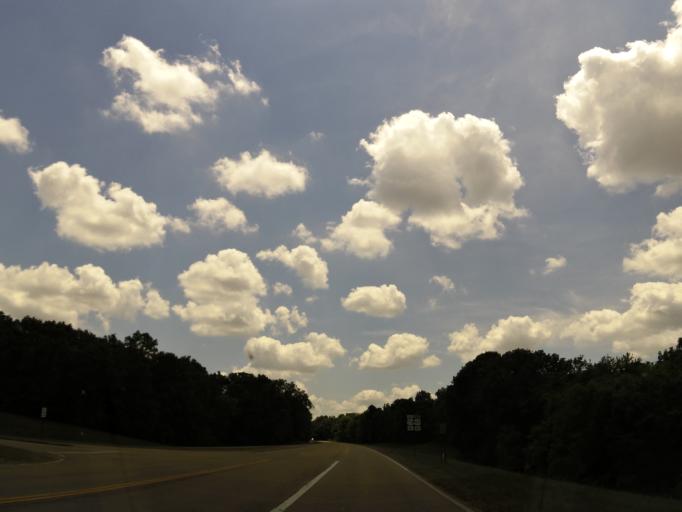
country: US
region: Mississippi
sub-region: Lee County
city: Tupelo
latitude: 34.2984
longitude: -88.7254
